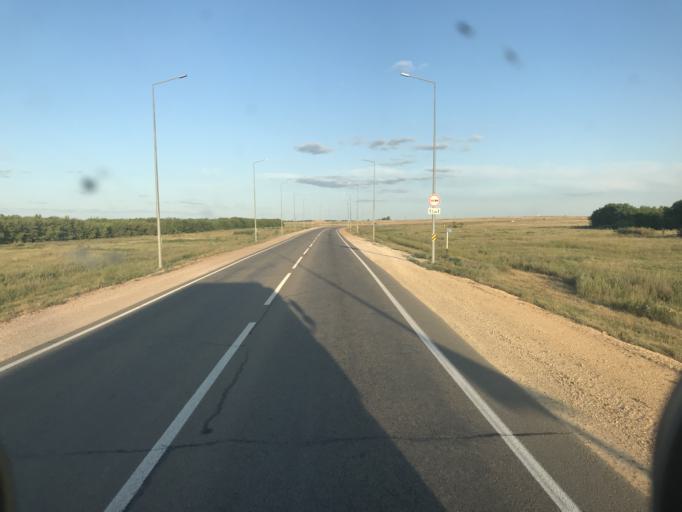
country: KZ
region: Astana Qalasy
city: Astana
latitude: 51.1843
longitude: 71.6057
